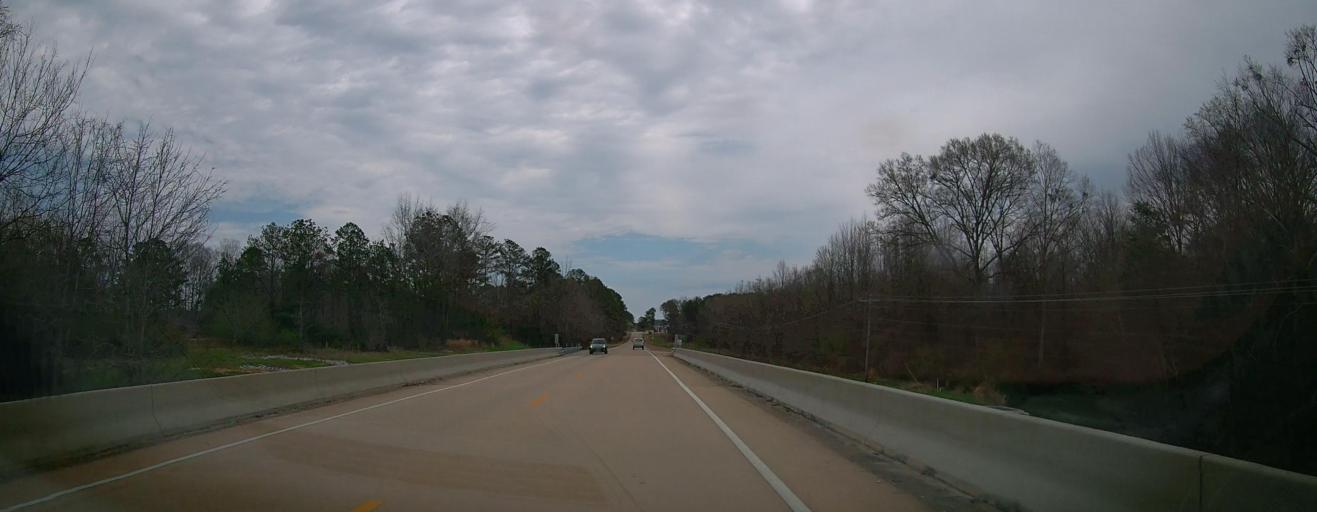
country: US
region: Mississippi
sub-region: Itawamba County
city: Fulton
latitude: 34.2392
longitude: -88.2716
